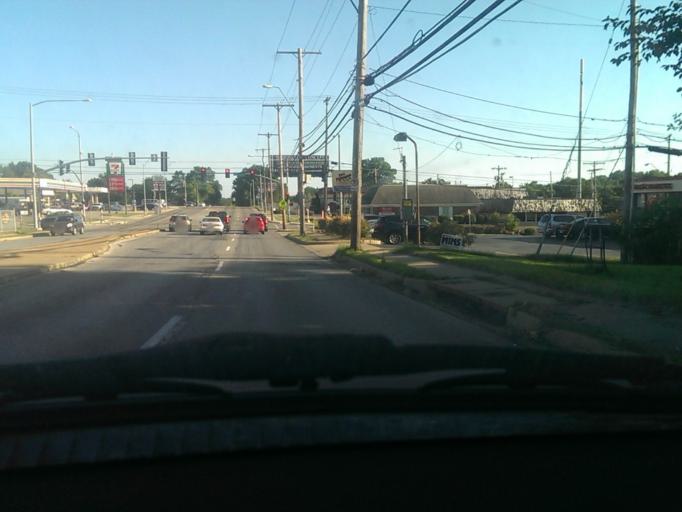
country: US
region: Kansas
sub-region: Johnson County
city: Leawood
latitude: 38.9676
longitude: -94.5954
